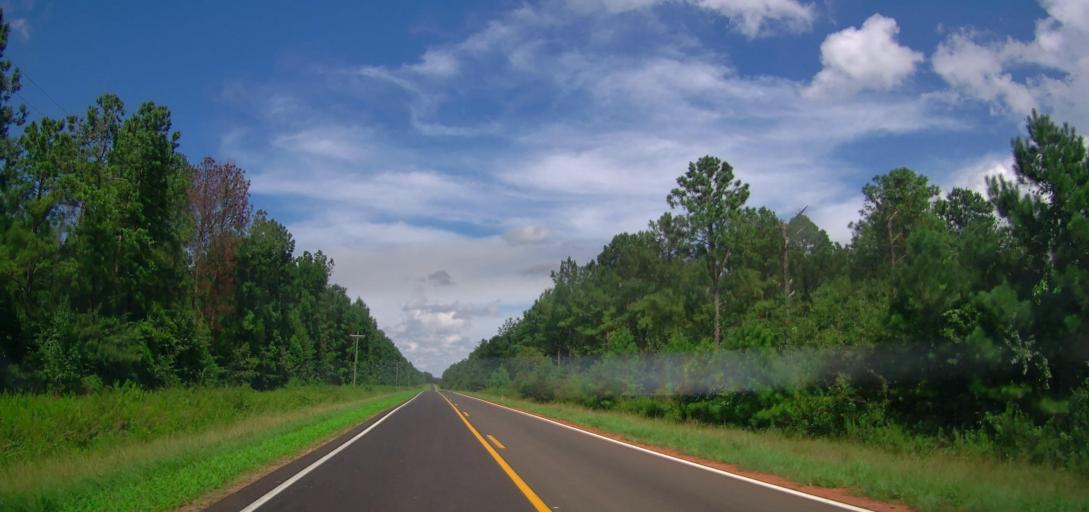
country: US
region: Georgia
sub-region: Macon County
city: Marshallville
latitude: 32.4650
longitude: -83.9038
